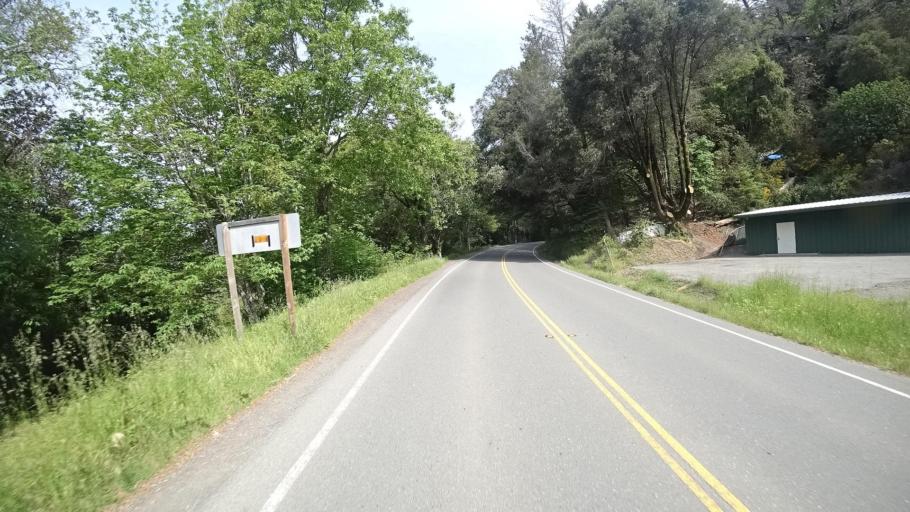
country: US
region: California
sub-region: Humboldt County
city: Redway
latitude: 40.1221
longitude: -123.8249
